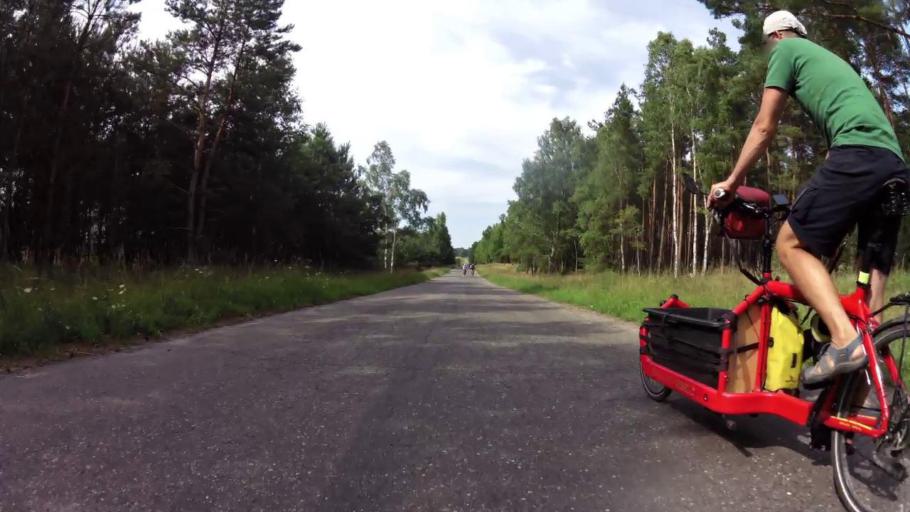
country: PL
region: West Pomeranian Voivodeship
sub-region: Powiat stargardzki
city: Insko
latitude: 53.4044
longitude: 15.6013
